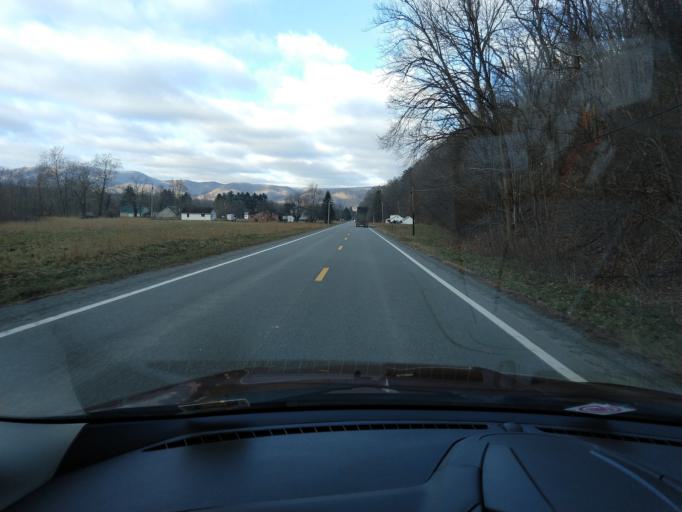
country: US
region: West Virginia
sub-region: Randolph County
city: Elkins
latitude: 38.6783
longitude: -79.9624
